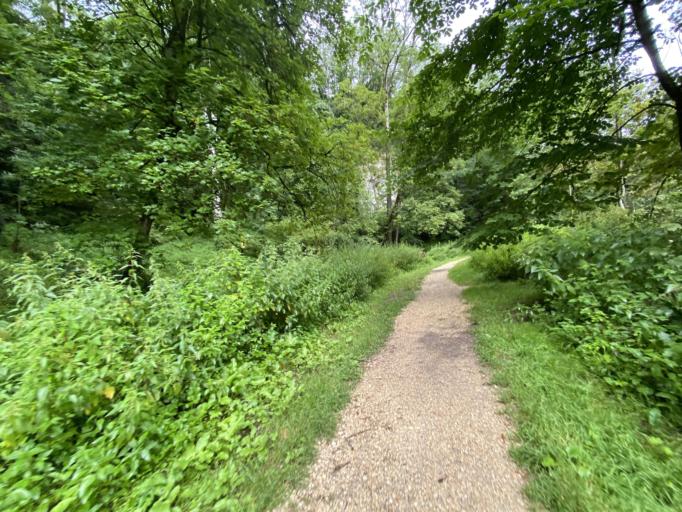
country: DE
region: Baden-Wuerttemberg
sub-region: Tuebingen Region
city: Bingen
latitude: 48.1071
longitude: 9.2572
